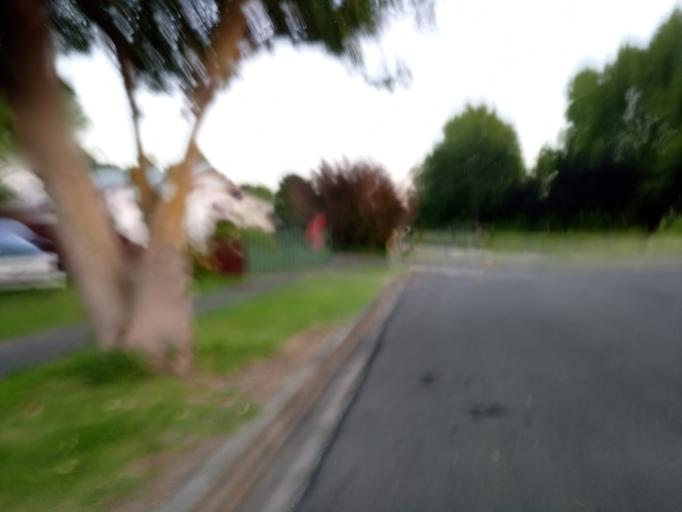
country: NZ
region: Gisborne
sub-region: Gisborne District
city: Gisborne
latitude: -38.6464
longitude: 177.9917
